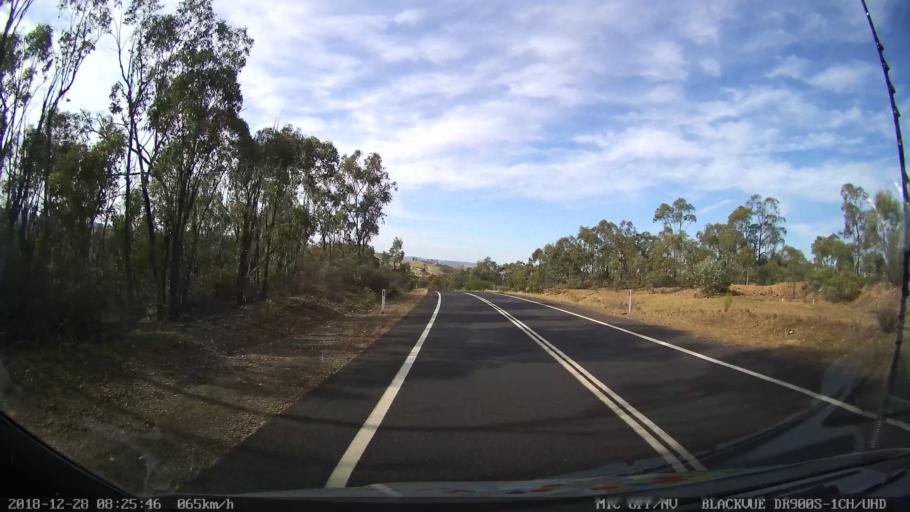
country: AU
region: New South Wales
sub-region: Blayney
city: Blayney
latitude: -33.9290
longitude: 149.3504
